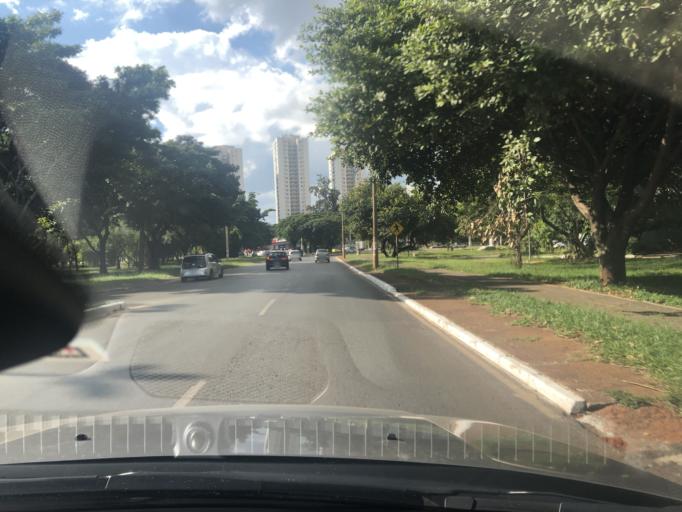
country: BR
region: Goias
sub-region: Luziania
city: Luziania
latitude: -16.0192
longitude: -48.0602
